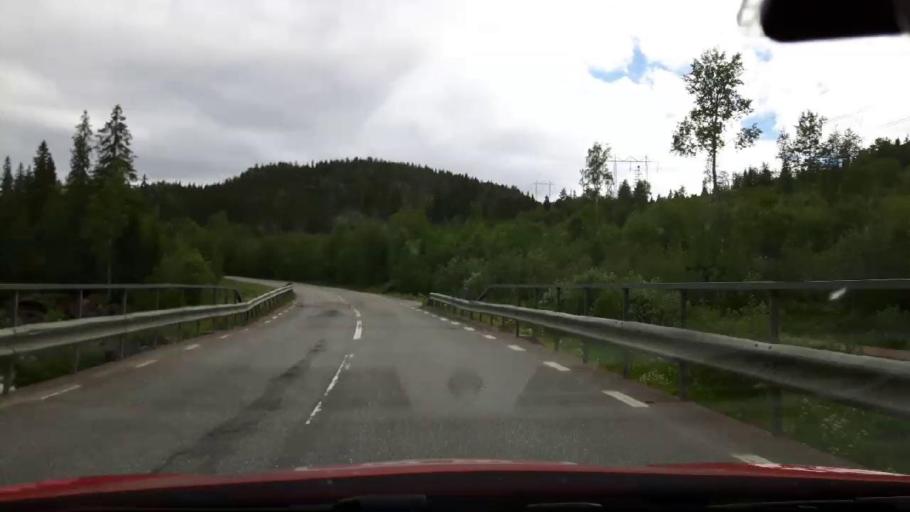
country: SE
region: Jaemtland
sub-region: Ragunda Kommun
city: Hammarstrand
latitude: 63.0504
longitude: 16.3789
